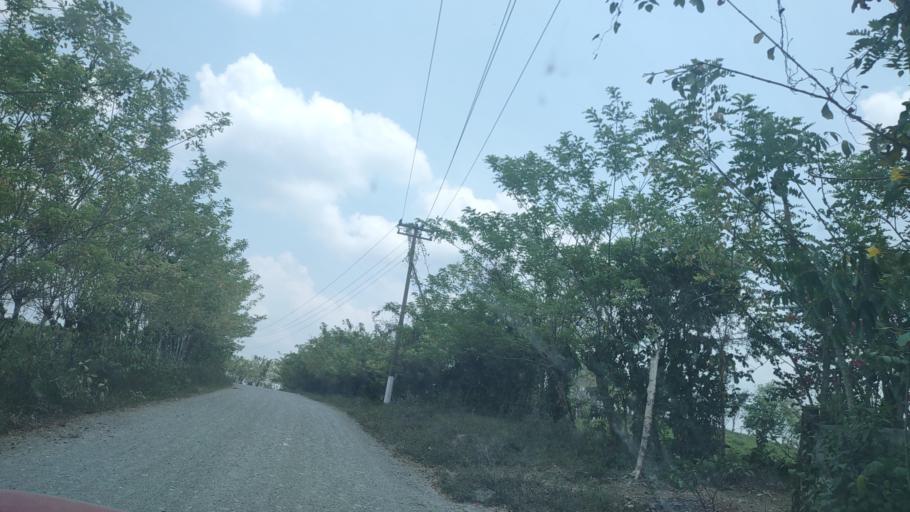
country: MX
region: Tabasco
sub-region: Huimanguillo
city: Francisco Rueda
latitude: 17.5874
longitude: -93.9586
